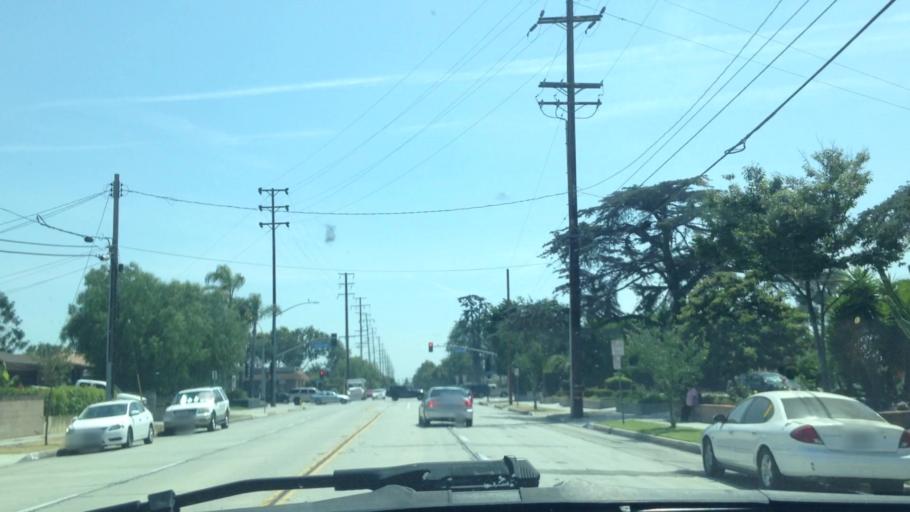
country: US
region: California
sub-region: Los Angeles County
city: Downey
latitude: 33.9224
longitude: -118.1461
